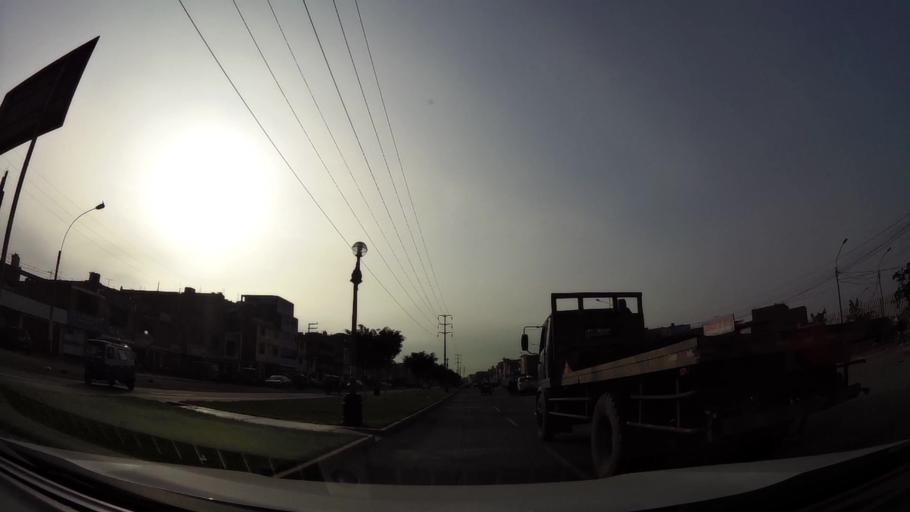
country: PE
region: Lima
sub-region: Lima
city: Independencia
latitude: -12.0030
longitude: -77.1004
